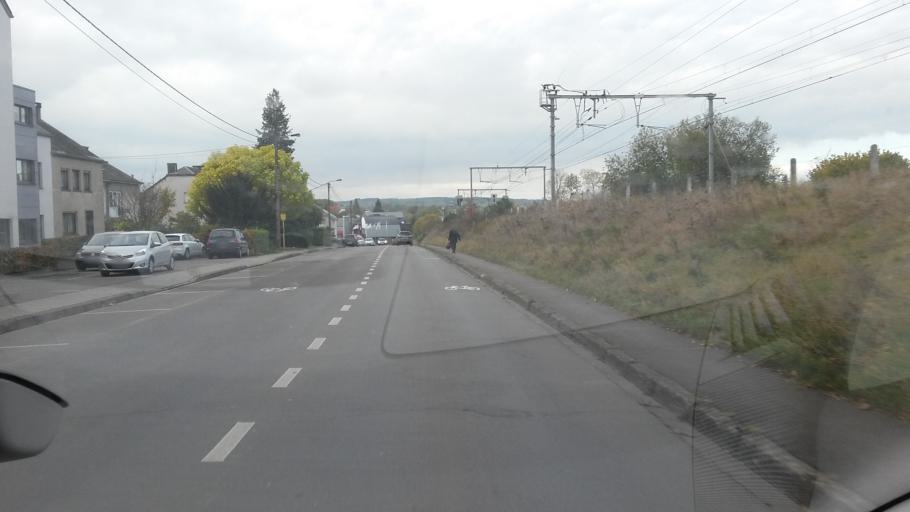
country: BE
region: Wallonia
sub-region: Province du Luxembourg
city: Arlon
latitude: 49.6826
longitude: 5.8009
